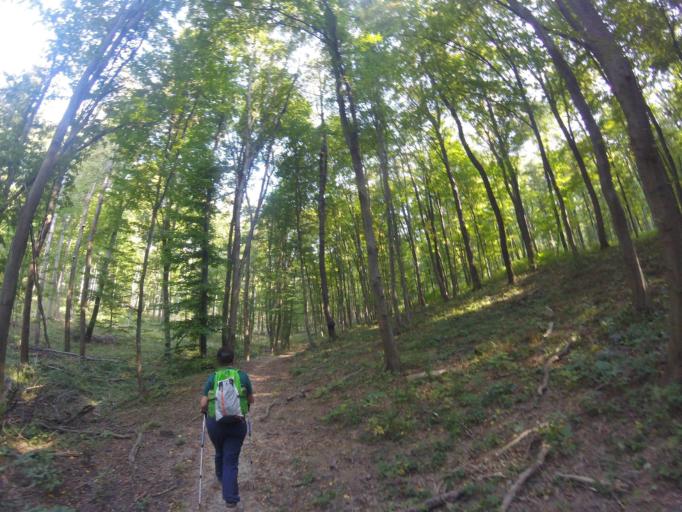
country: HU
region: Komarom-Esztergom
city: Piliscsev
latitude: 47.7127
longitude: 18.8445
